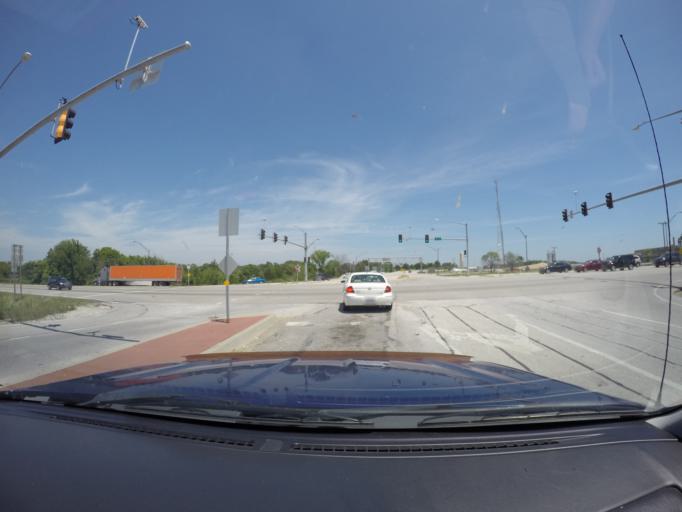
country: US
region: Kansas
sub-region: Wyandotte County
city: Bonner Springs
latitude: 39.0994
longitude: -94.8821
